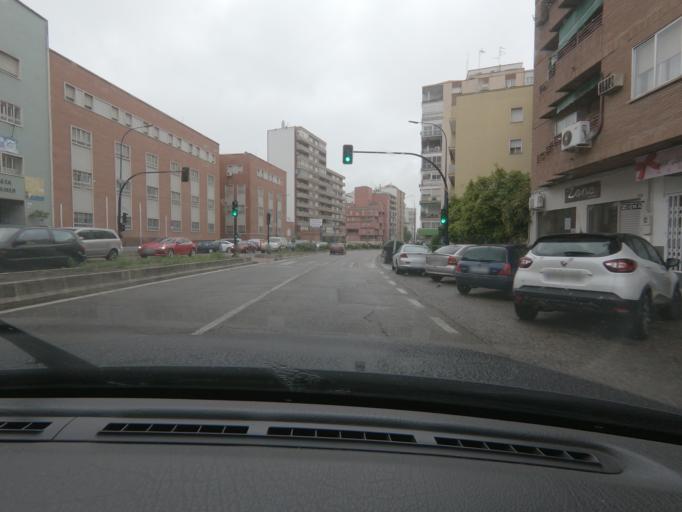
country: ES
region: Extremadura
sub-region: Provincia de Badajoz
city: Badajoz
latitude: 38.8694
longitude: -6.9756
